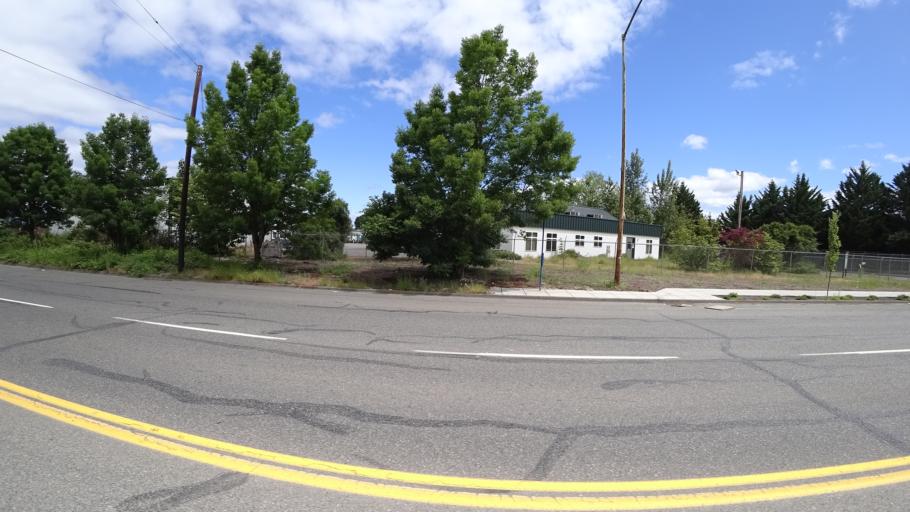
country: US
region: Oregon
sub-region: Washington County
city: West Haven
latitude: 45.6007
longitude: -122.7425
